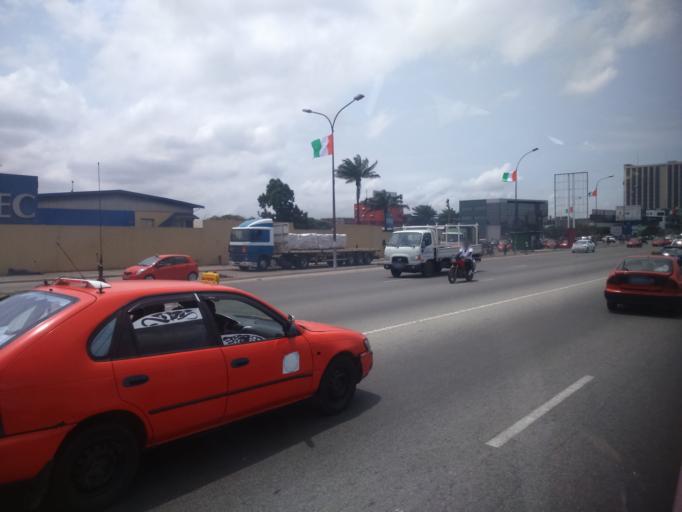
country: CI
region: Lagunes
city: Abidjan
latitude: 5.3010
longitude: -3.9905
